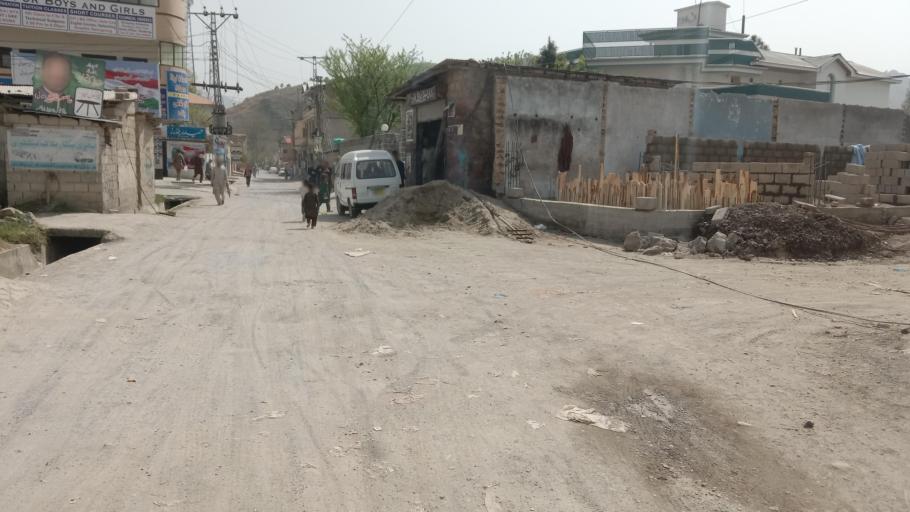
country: PK
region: Khyber Pakhtunkhwa
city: Abbottabad
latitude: 34.1571
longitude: 73.2594
